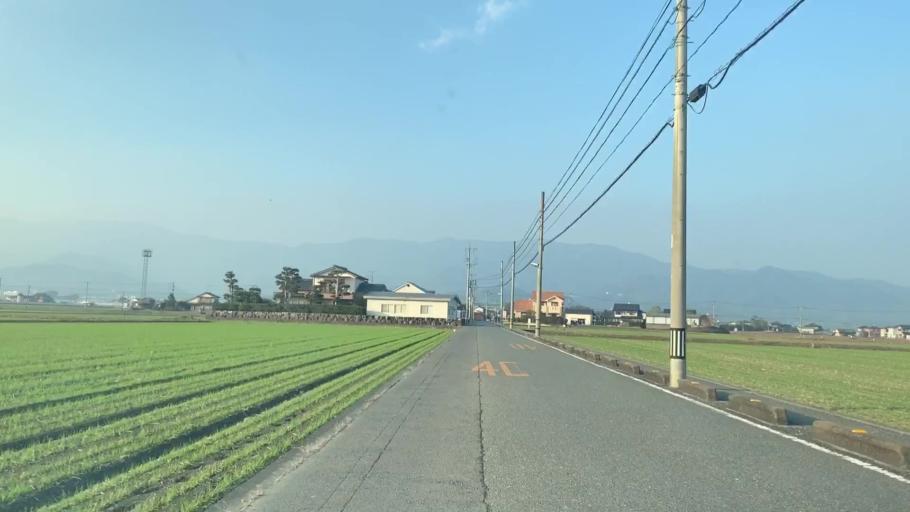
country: JP
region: Saga Prefecture
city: Saga-shi
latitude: 33.2745
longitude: 130.2277
